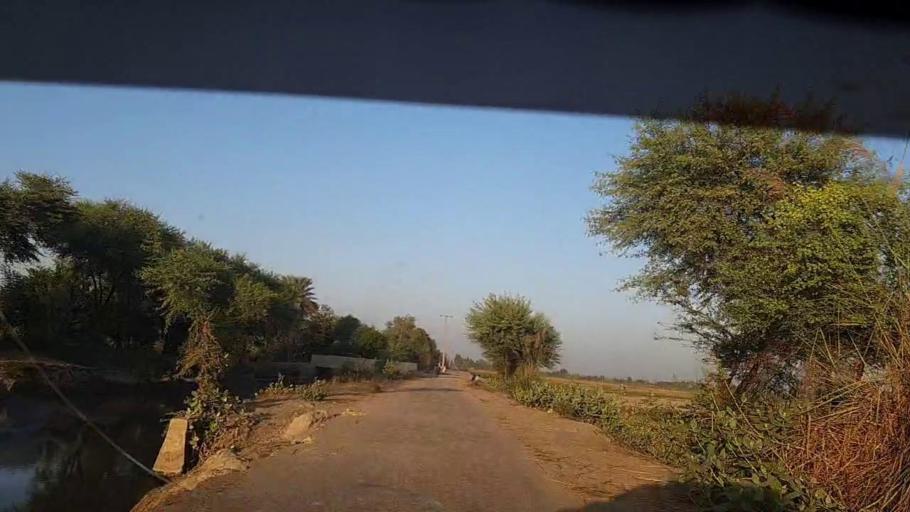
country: PK
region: Sindh
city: Ratodero
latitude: 27.8880
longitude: 68.2161
